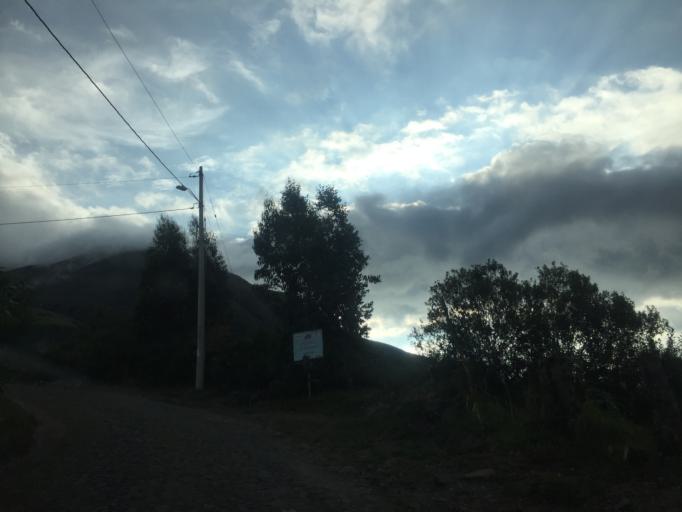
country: EC
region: Imbabura
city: Ibarra
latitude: 0.2856
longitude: -78.1381
